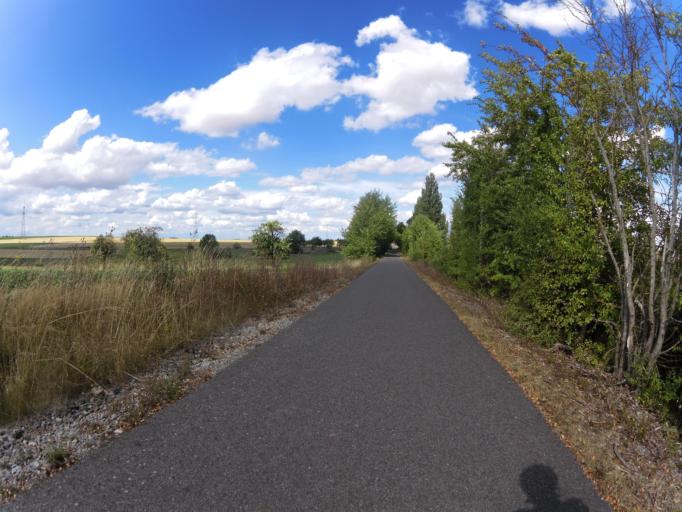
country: DE
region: Bavaria
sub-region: Regierungsbezirk Unterfranken
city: Sonderhofen
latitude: 49.6087
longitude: 10.0069
